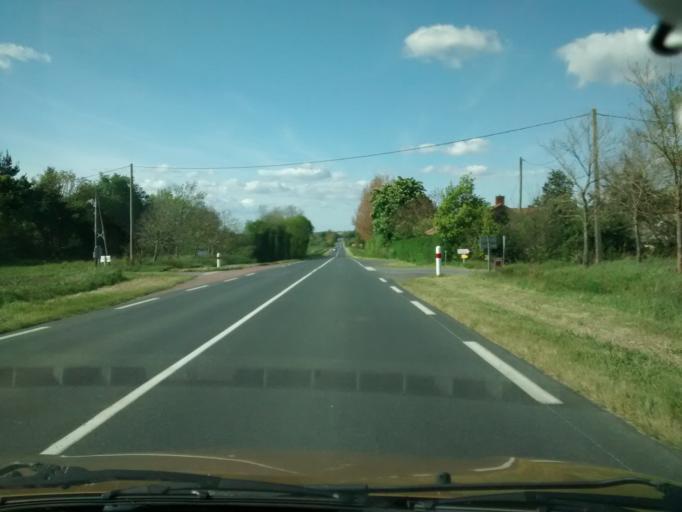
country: FR
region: Pays de la Loire
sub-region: Departement de la Vendee
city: Saint-Philbert-de-Bouaine
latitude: 46.9654
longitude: -1.5159
